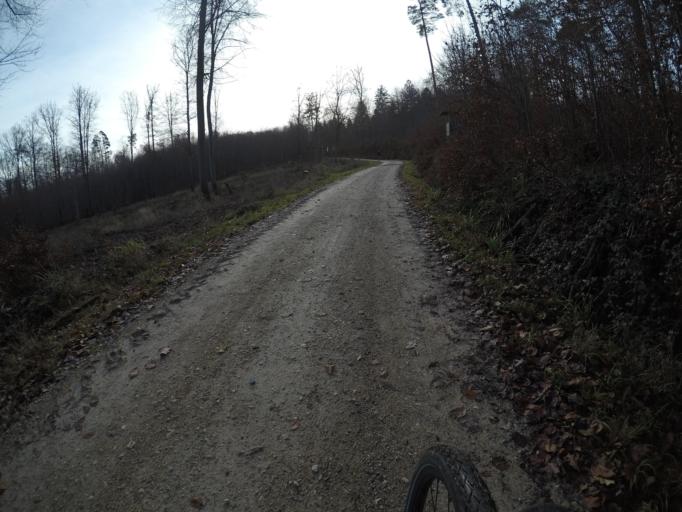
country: DE
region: Baden-Wuerttemberg
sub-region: Regierungsbezirk Stuttgart
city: Esslingen
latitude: 48.7573
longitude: 9.3483
